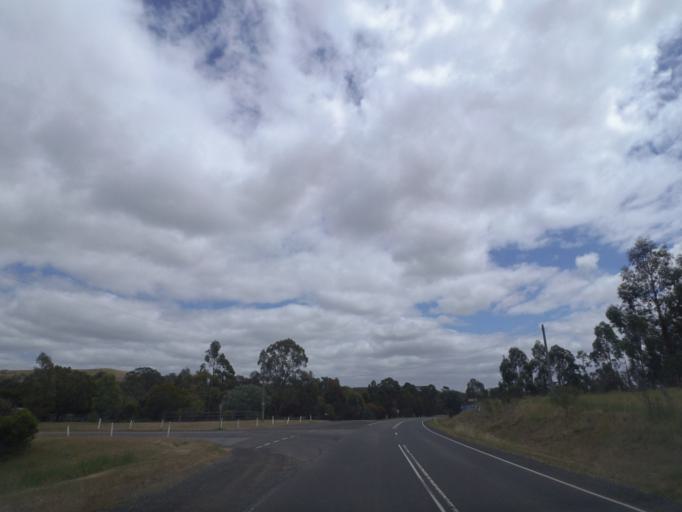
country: AU
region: Victoria
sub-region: Whittlesea
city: Whittlesea
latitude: -37.2851
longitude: 145.0525
